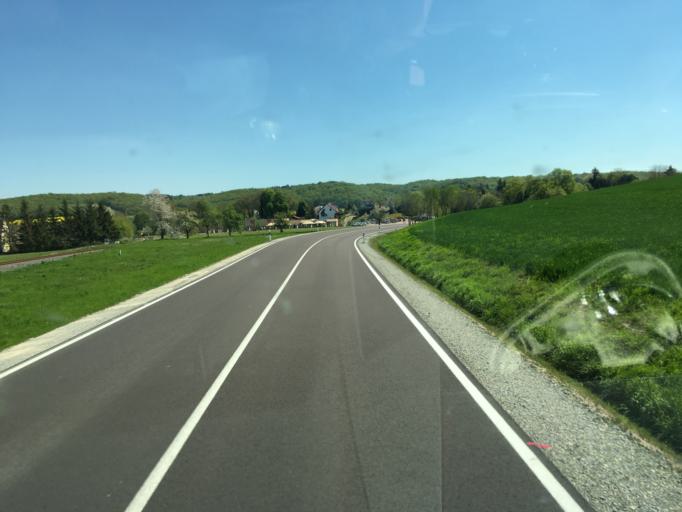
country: DE
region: Saxony-Anhalt
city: Balgstadt
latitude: 51.2093
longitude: 11.7260
